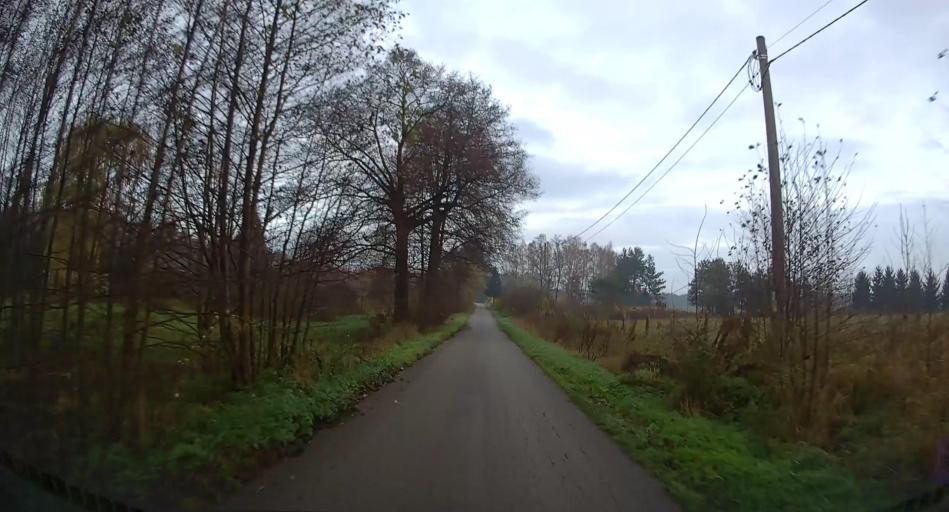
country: PL
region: Lodz Voivodeship
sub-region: Powiat skierniewicki
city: Kowiesy
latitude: 51.9351
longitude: 20.4020
